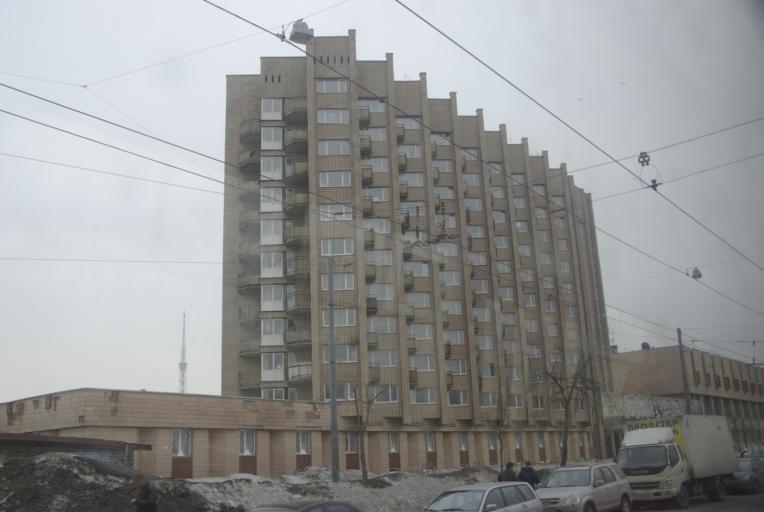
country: RU
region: Leningrad
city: Sampsonievskiy
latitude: 59.9748
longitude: 30.3461
